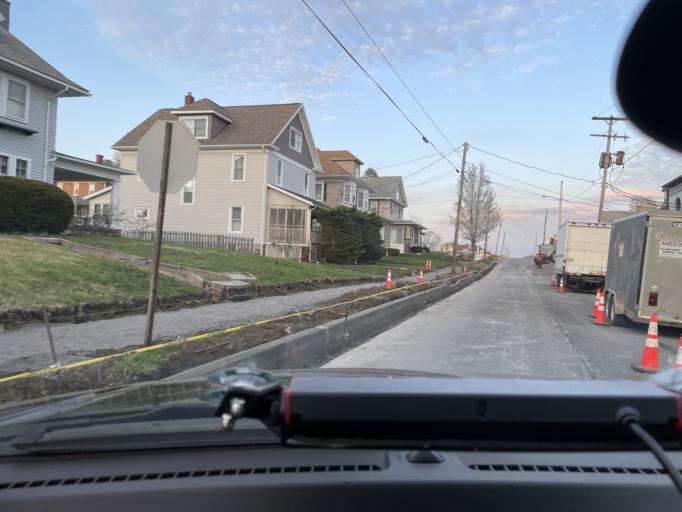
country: US
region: Pennsylvania
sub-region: Cambria County
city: Ebensburg
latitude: 40.4878
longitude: -78.7291
